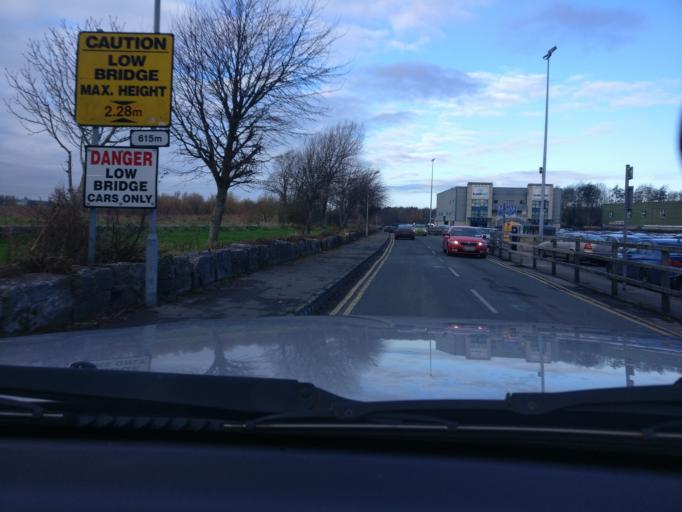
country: IE
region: Connaught
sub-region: County Galway
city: Gaillimh
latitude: 53.2791
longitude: -9.0521
